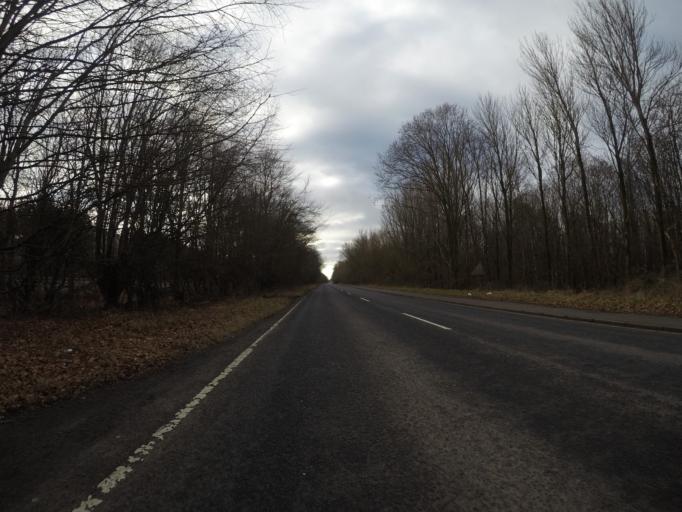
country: GB
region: Scotland
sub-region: North Ayrshire
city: Dreghorn
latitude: 55.5821
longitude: -4.6450
